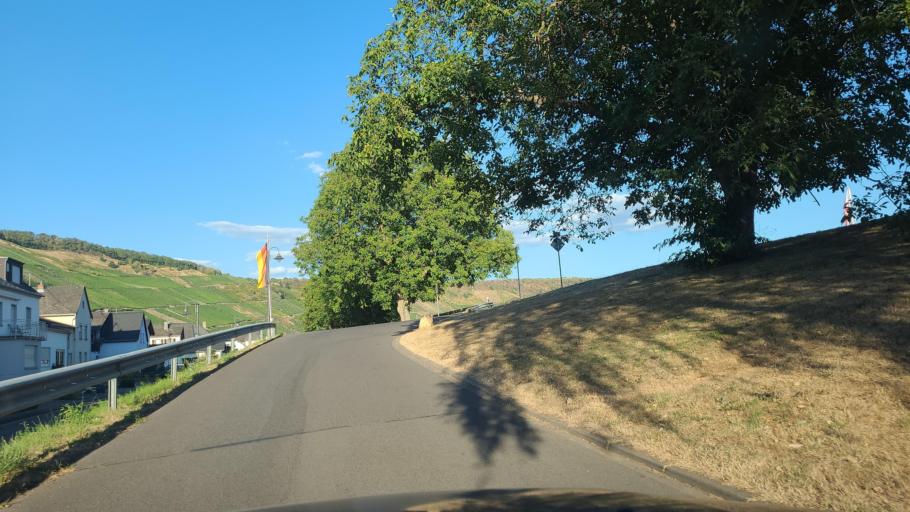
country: DE
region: Rheinland-Pfalz
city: Klusserath
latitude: 49.8438
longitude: 6.8572
